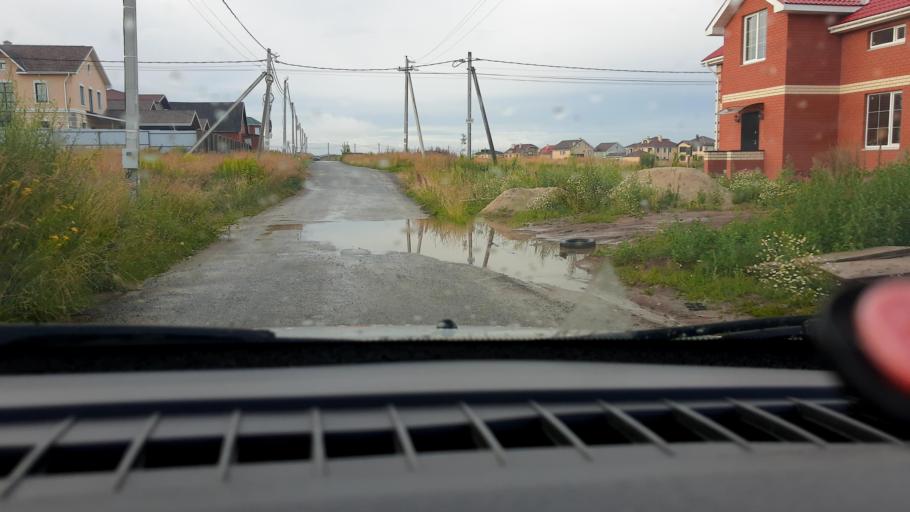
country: RU
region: Nizjnij Novgorod
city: Nizhniy Novgorod
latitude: 56.2161
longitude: 43.9662
